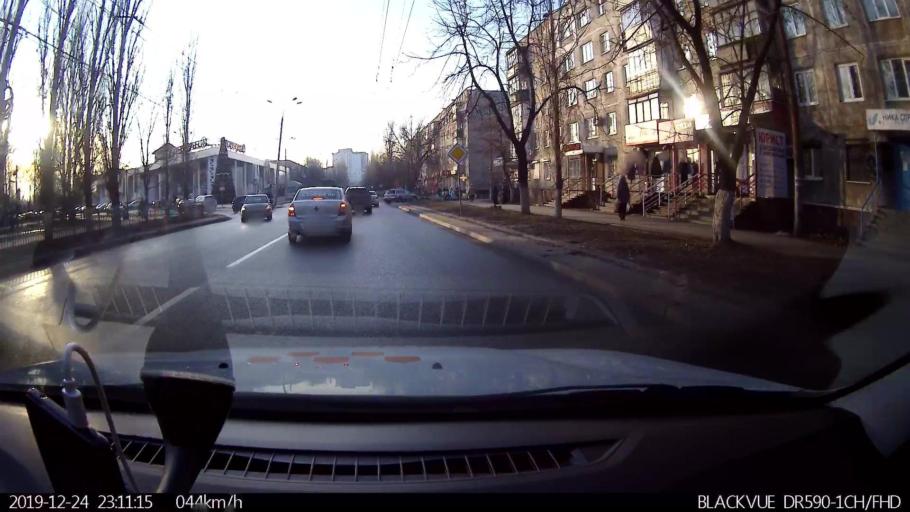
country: RU
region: Nizjnij Novgorod
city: Gorbatovka
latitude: 56.2599
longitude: 43.8766
